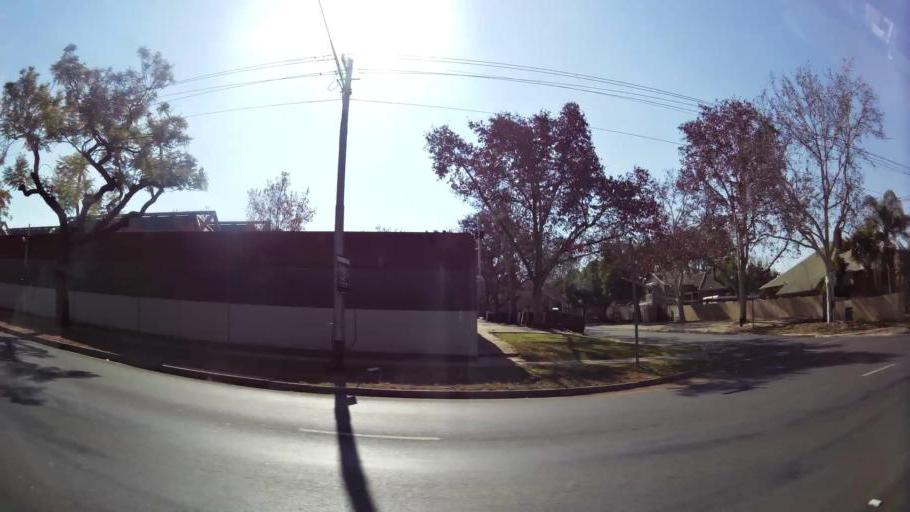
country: ZA
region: Gauteng
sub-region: City of Tshwane Metropolitan Municipality
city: Pretoria
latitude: -25.7451
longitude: 28.2293
